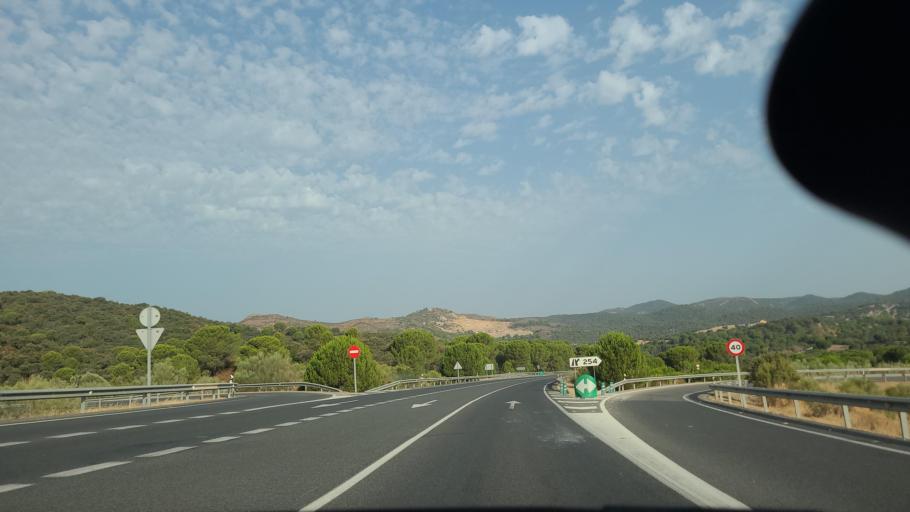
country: ES
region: Andalusia
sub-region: Province of Cordoba
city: Cordoba
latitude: 37.9962
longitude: -4.7940
